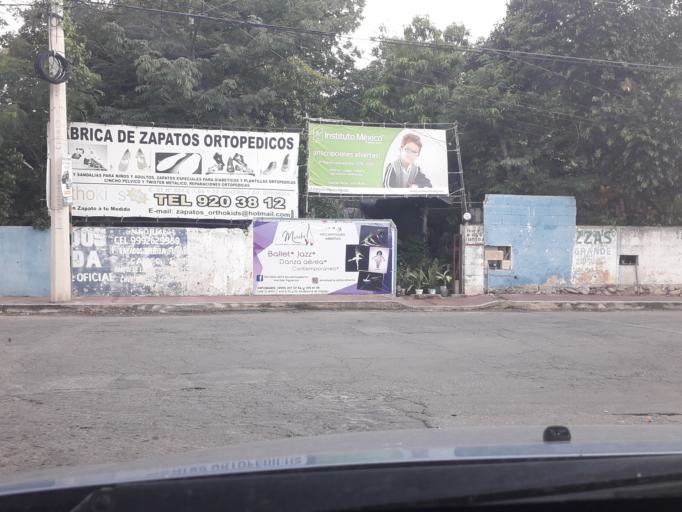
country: MX
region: Yucatan
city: Merida
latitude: 21.0086
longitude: -89.6367
